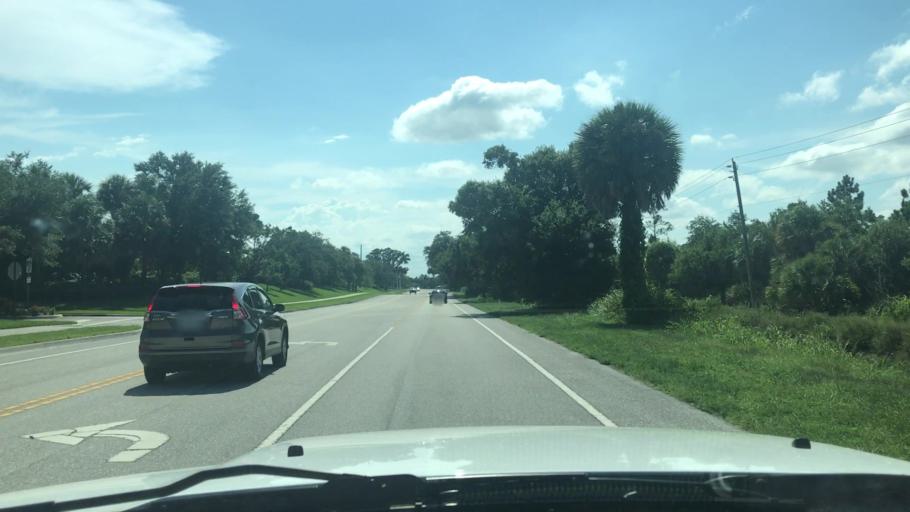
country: US
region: Florida
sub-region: Indian River County
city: Florida Ridge
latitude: 27.5722
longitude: -80.4100
